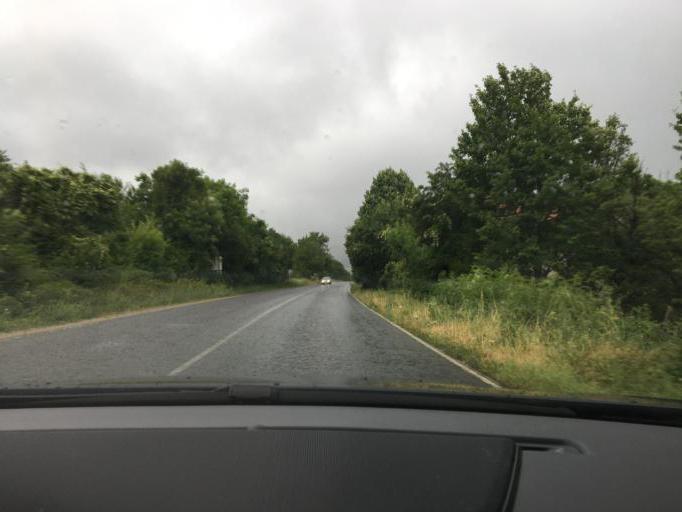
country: MK
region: Kriva Palanka
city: Kriva Palanka
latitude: 42.2357
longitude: 22.5038
